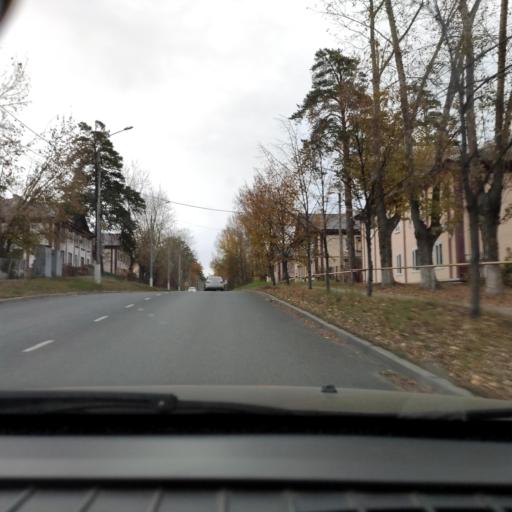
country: RU
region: Samara
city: Tol'yatti
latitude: 53.4765
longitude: 49.3686
